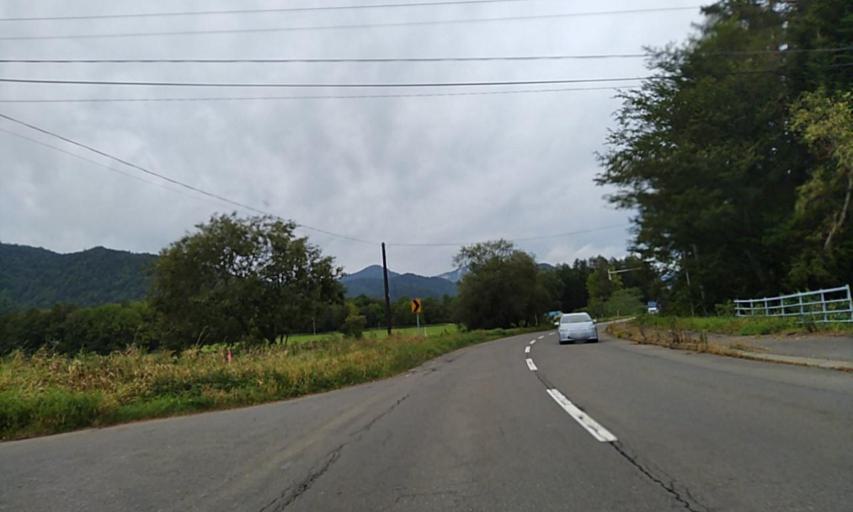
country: JP
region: Hokkaido
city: Bihoro
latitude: 43.5536
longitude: 144.3329
